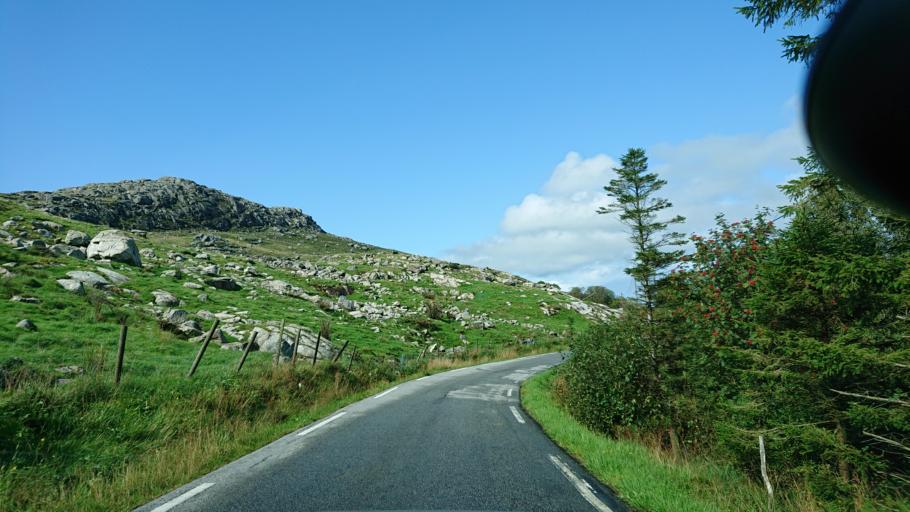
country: NO
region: Rogaland
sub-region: Gjesdal
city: Algard
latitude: 58.6983
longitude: 5.8892
